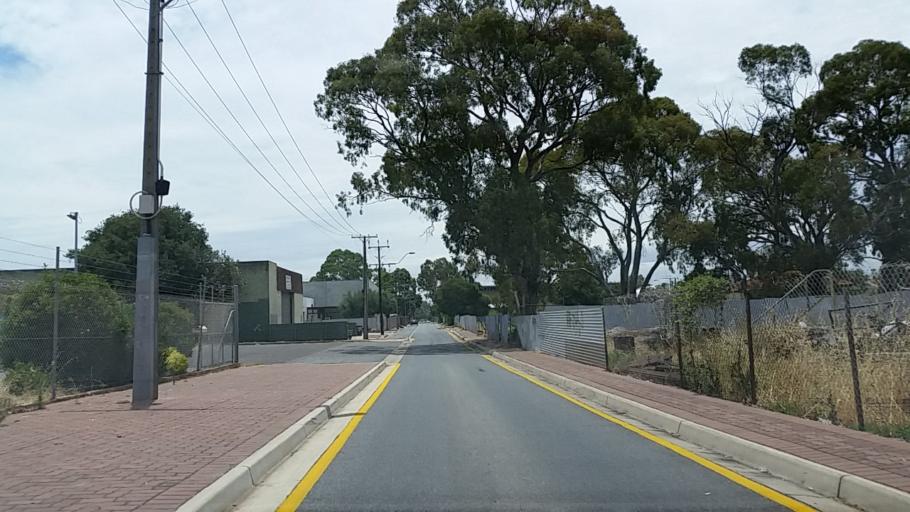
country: AU
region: South Australia
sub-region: Charles Sturt
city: Allenby Gardens
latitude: -34.8966
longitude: 138.5466
